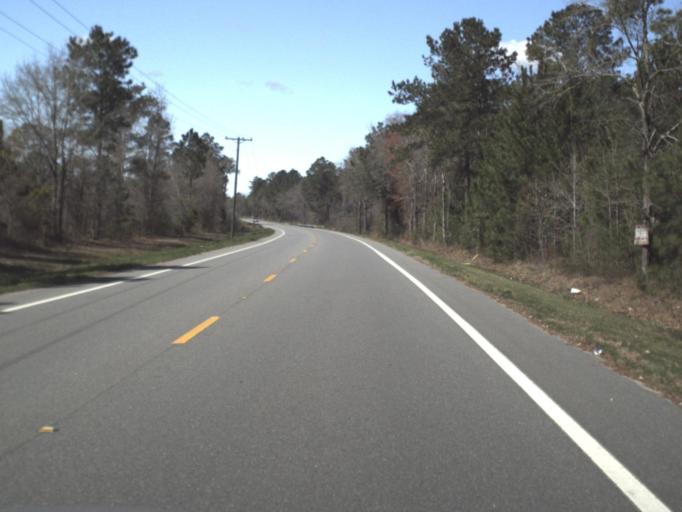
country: US
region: Florida
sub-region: Gadsden County
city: Gretna
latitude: 30.6500
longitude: -84.6818
